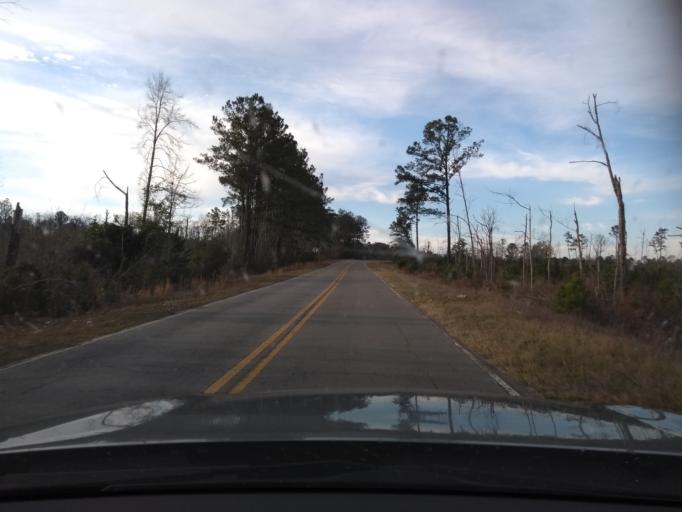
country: US
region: Georgia
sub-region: Evans County
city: Claxton
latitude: 32.2252
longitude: -81.7691
